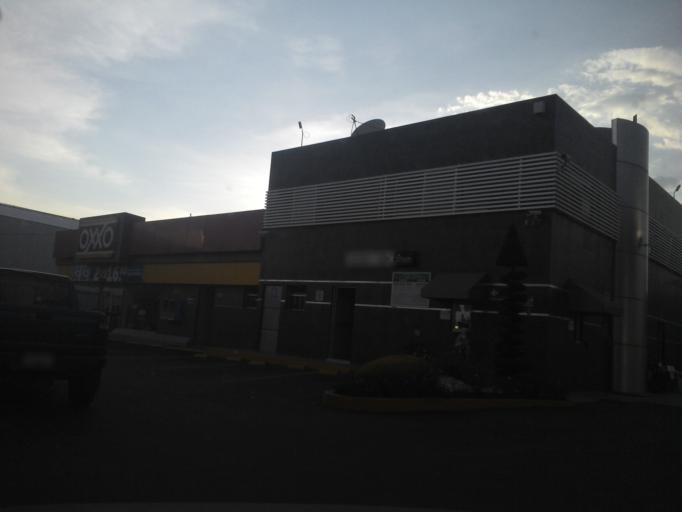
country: MX
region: Jalisco
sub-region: Zapotlanejo
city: La Mezquitera
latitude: 20.5885
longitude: -103.1151
